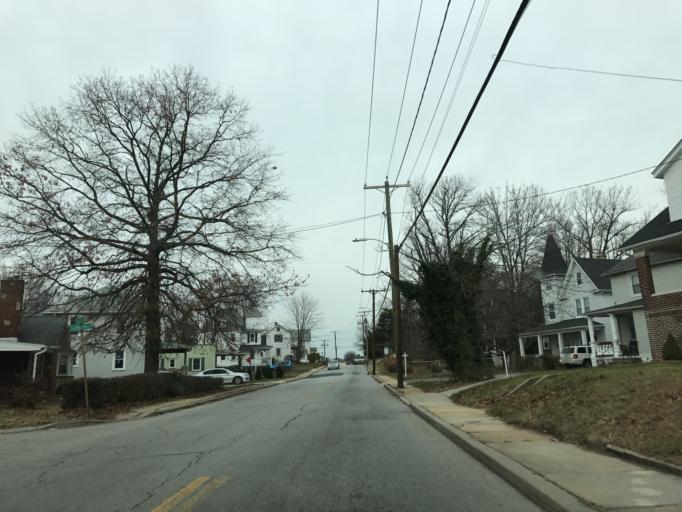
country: US
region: Maryland
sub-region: Baltimore County
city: Parkville
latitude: 39.3493
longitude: -76.5588
